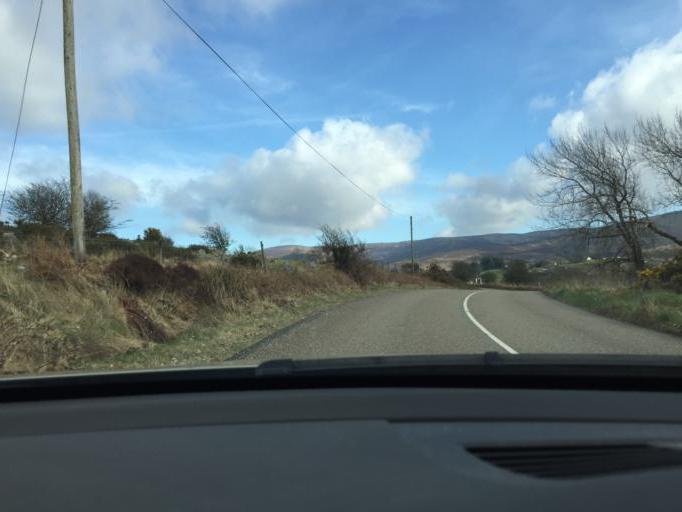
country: IE
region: Leinster
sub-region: Wicklow
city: Valleymount
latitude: 53.0613
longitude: -6.5062
